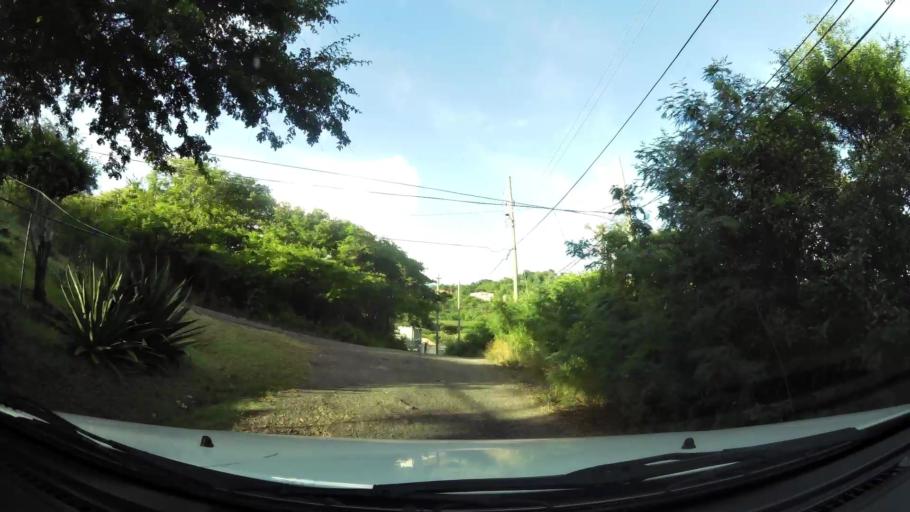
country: LC
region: Gros-Islet
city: Gros Islet
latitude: 14.0966
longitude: -60.9306
